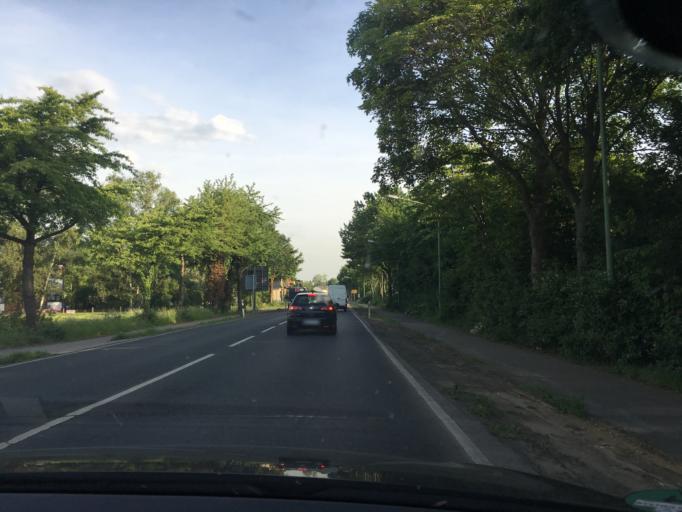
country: DE
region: North Rhine-Westphalia
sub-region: Regierungsbezirk Koln
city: Niederzier
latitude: 50.8506
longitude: 6.4440
